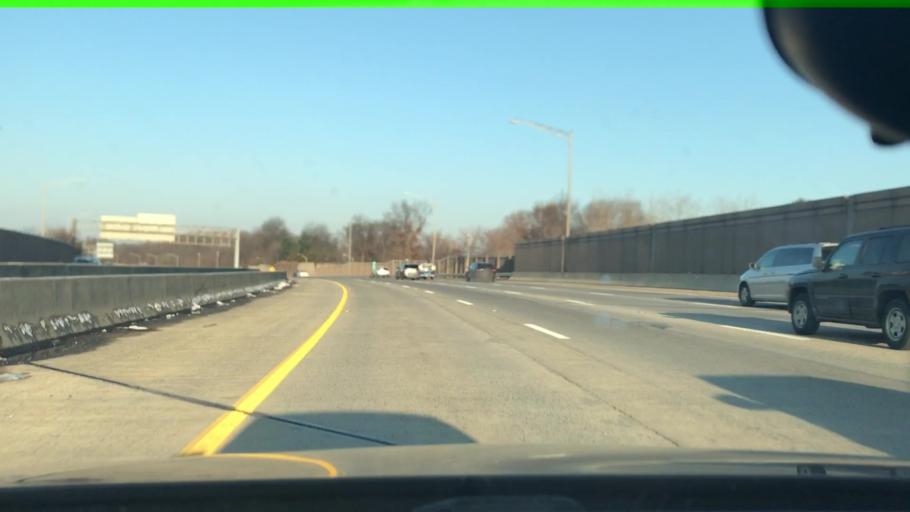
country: US
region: New Jersey
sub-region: Bergen County
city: Rochelle Park
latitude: 40.9000
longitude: -74.0820
